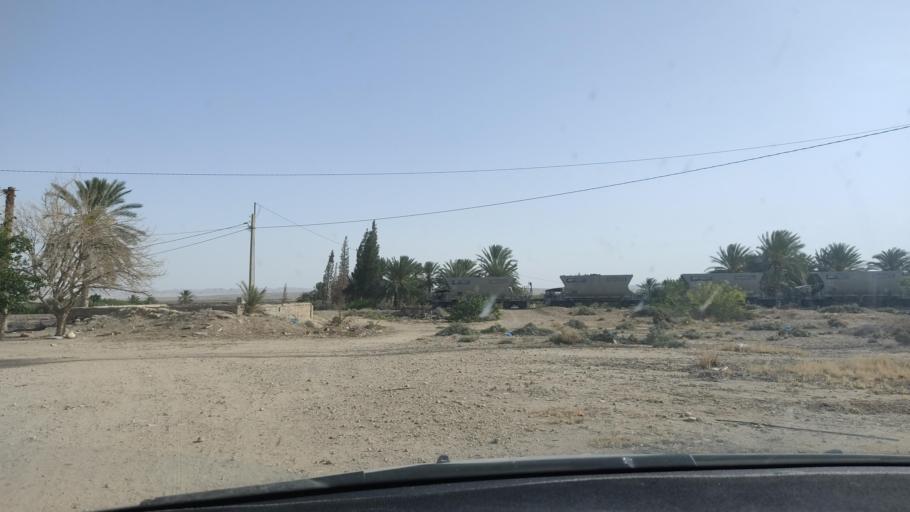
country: TN
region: Gafsa
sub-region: Gafsa Municipality
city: Gafsa
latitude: 34.3518
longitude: 8.8626
